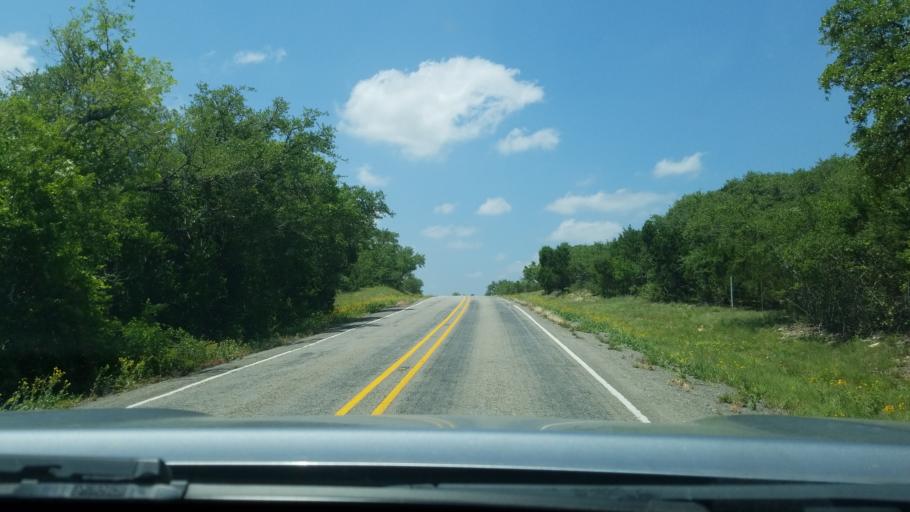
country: US
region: Texas
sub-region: Hays County
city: Woodcreek
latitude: 30.0574
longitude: -98.2068
